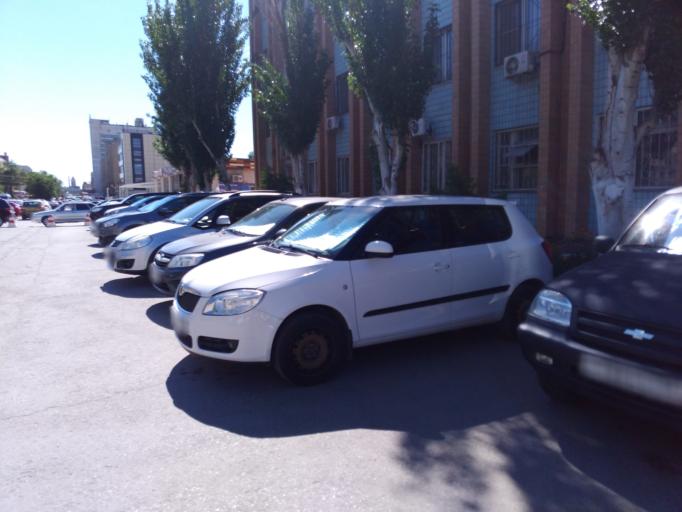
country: RU
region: Volgograd
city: Volgograd
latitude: 48.7148
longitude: 44.5211
